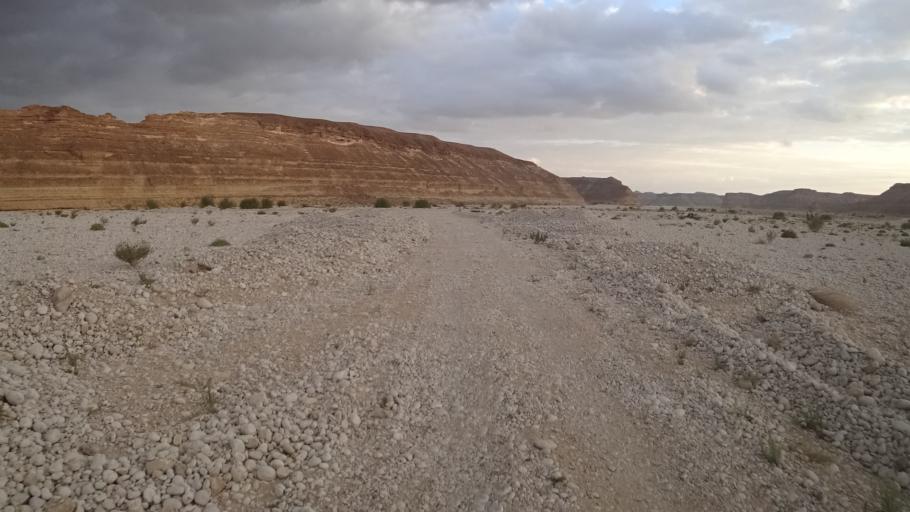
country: YE
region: Al Mahrah
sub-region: Shahan
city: Shihan as Sufla
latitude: 17.3295
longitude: 52.9206
